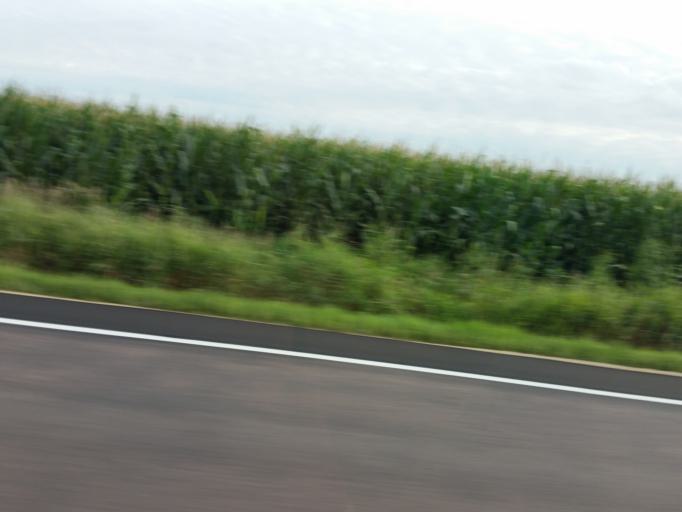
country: US
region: Minnesota
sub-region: Goodhue County
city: Cannon Falls
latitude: 44.6013
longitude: -92.9702
